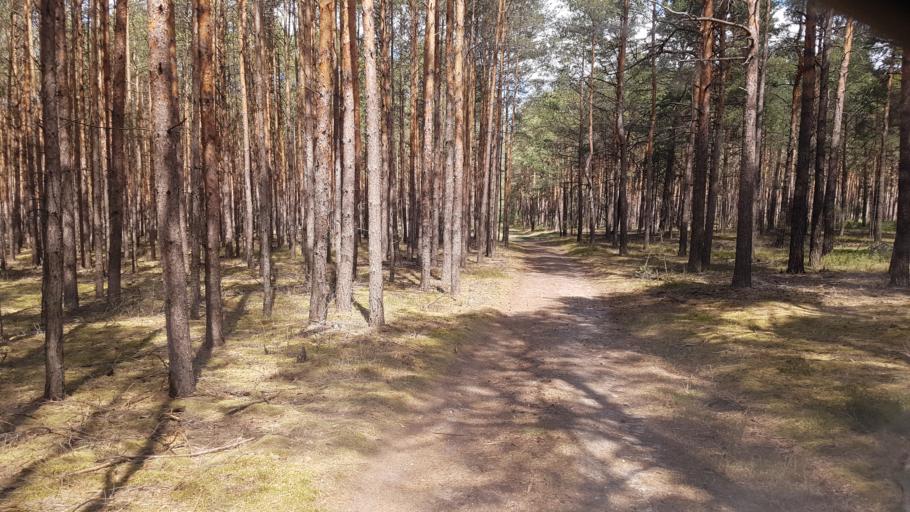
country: DE
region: Brandenburg
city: Sonnewalde
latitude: 51.6462
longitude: 13.6590
